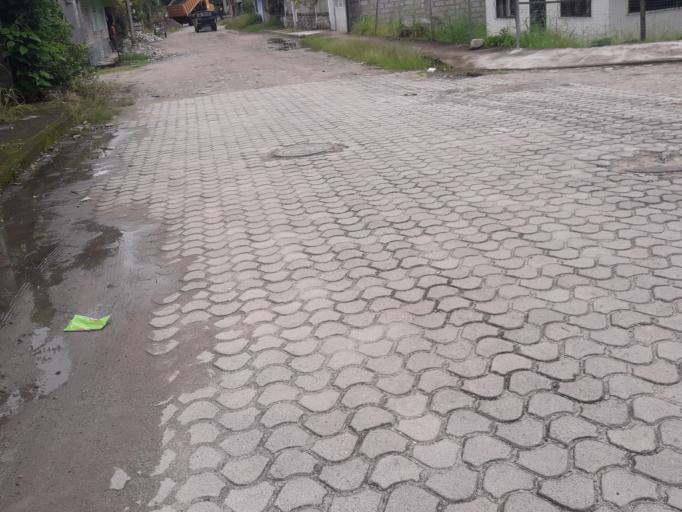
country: EC
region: Napo
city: Tena
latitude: -0.9859
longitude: -77.8304
